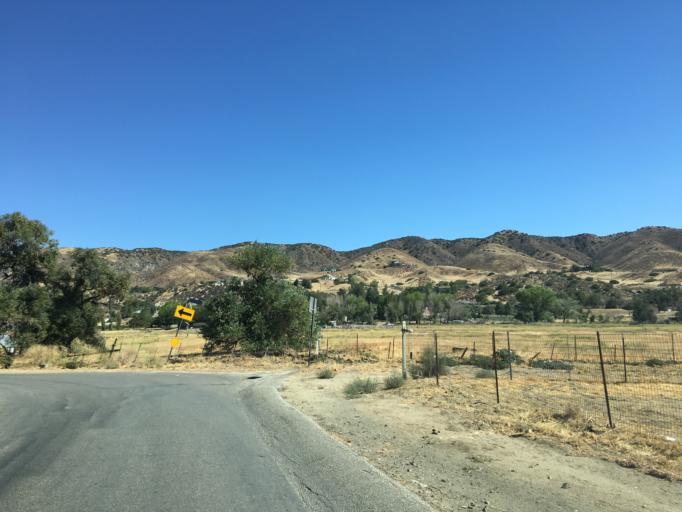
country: US
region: California
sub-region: Los Angeles County
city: Leona Valley
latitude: 34.6123
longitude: -118.2843
